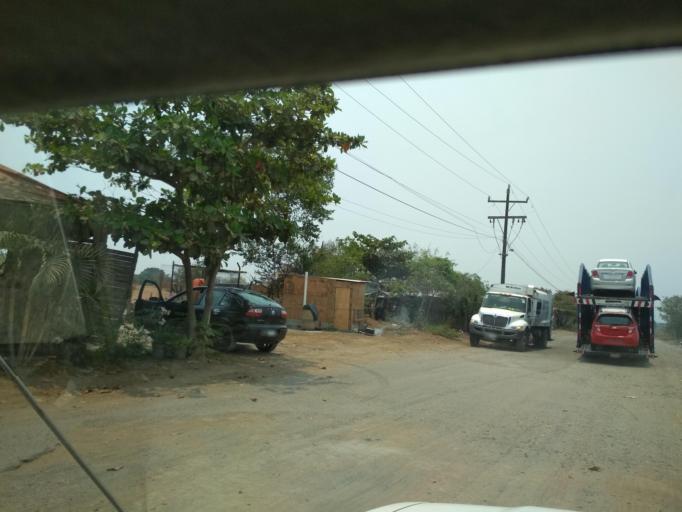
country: MX
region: Veracruz
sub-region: Veracruz
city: Delfino Victoria (Santa Fe)
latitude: 19.2024
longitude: -96.2674
